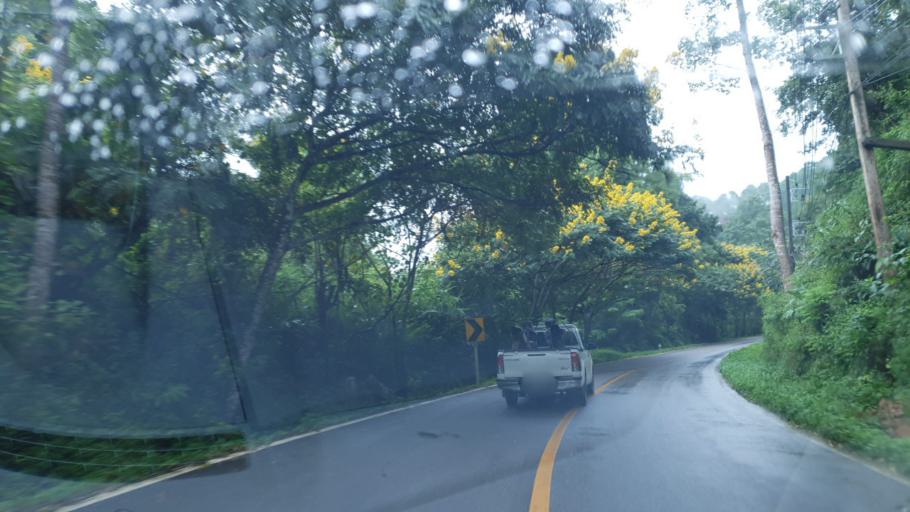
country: TH
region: Mae Hong Son
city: Ban Huai I Huak
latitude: 18.1623
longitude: 98.0505
